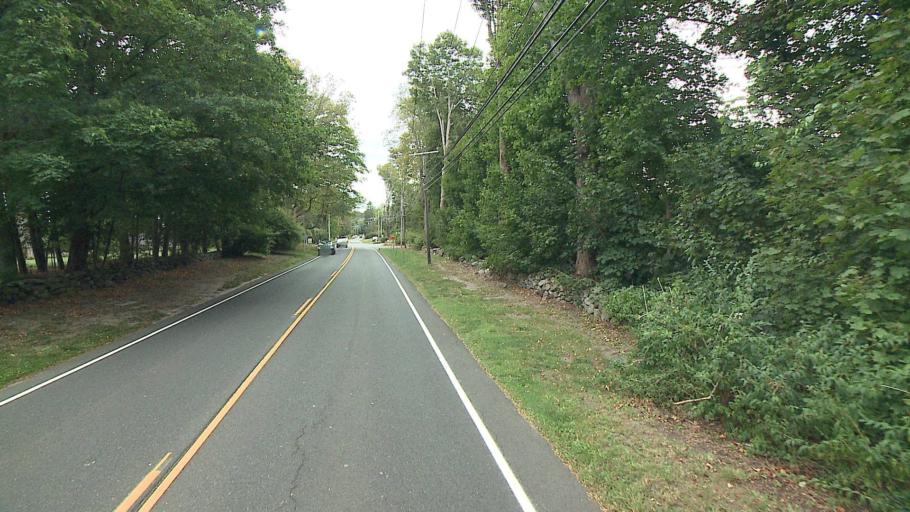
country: US
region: Connecticut
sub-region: Fairfield County
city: Wilton
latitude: 41.2229
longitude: -73.4766
